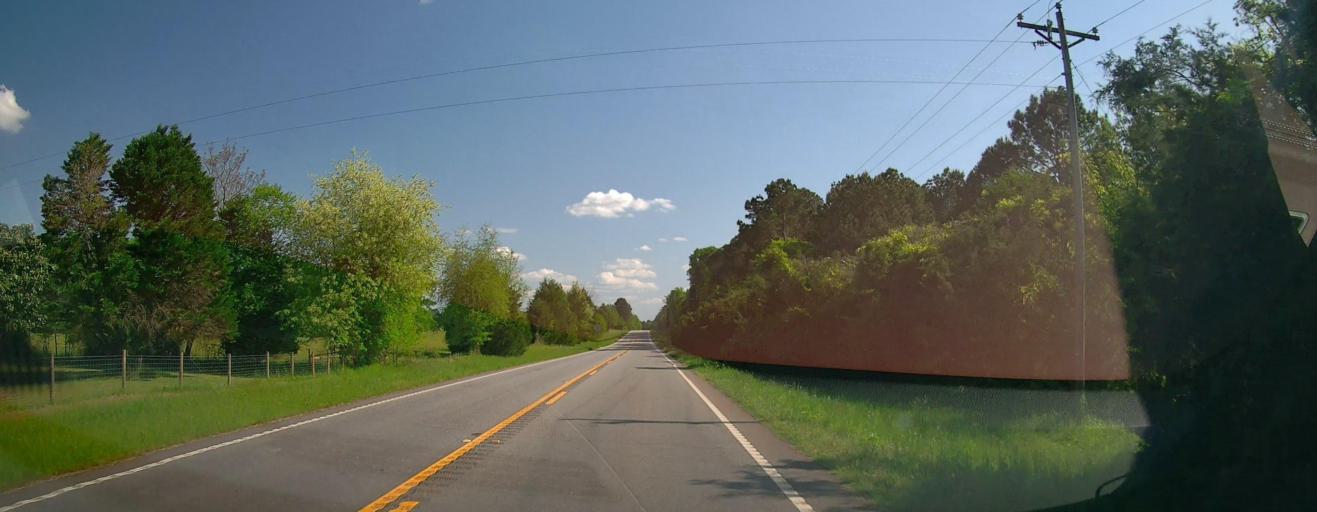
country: US
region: Georgia
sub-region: Morgan County
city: Madison
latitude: 33.6588
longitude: -83.4972
